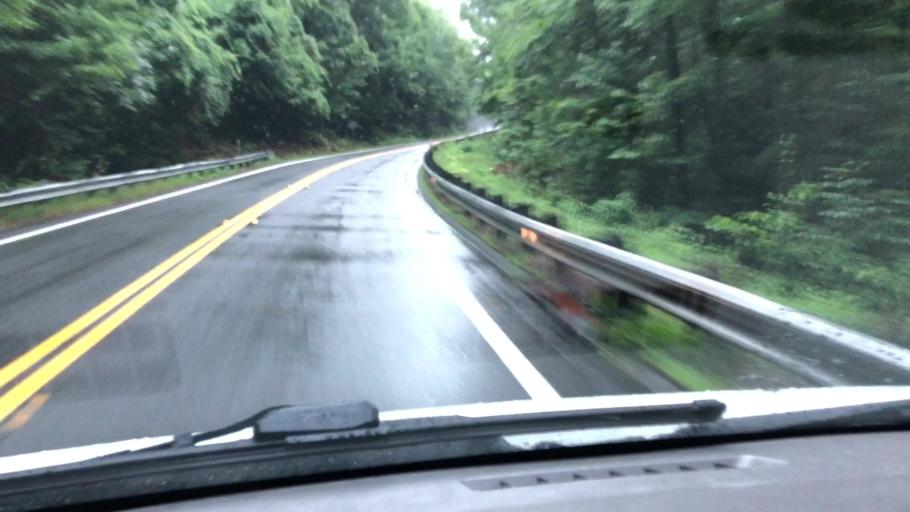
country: US
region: Massachusetts
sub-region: Hampshire County
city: Westhampton
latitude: 42.2998
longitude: -72.8674
